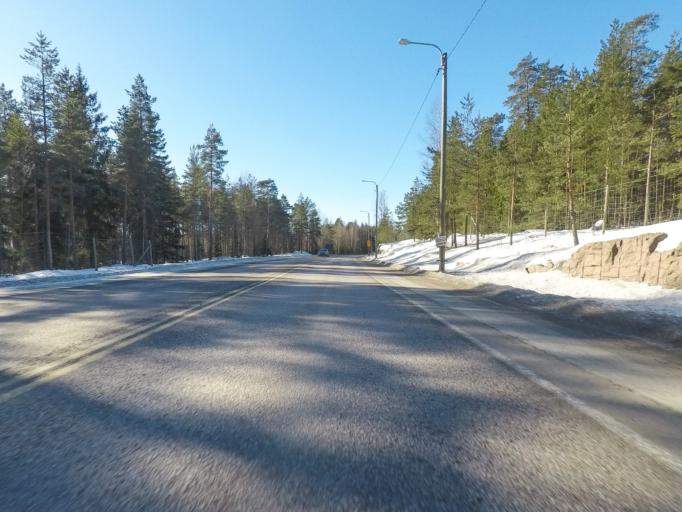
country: FI
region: Uusimaa
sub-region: Helsinki
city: Kirkkonummi
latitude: 60.2721
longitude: 24.4513
